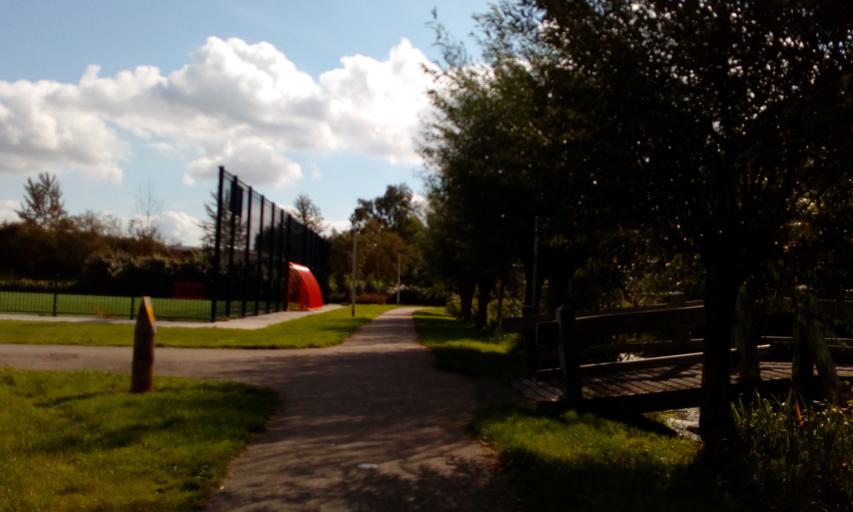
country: NL
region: South Holland
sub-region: Gemeente Gouda
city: Bloemendaal
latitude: 51.9917
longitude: 4.6709
